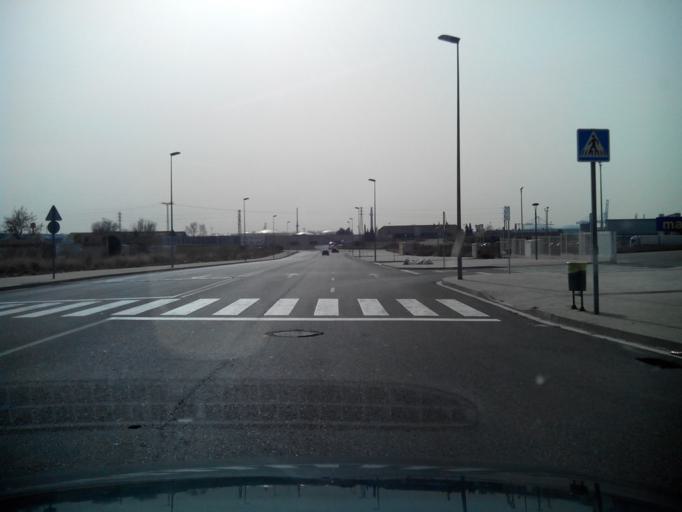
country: ES
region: Catalonia
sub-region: Provincia de Tarragona
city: Constanti
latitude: 41.1150
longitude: 1.2103
